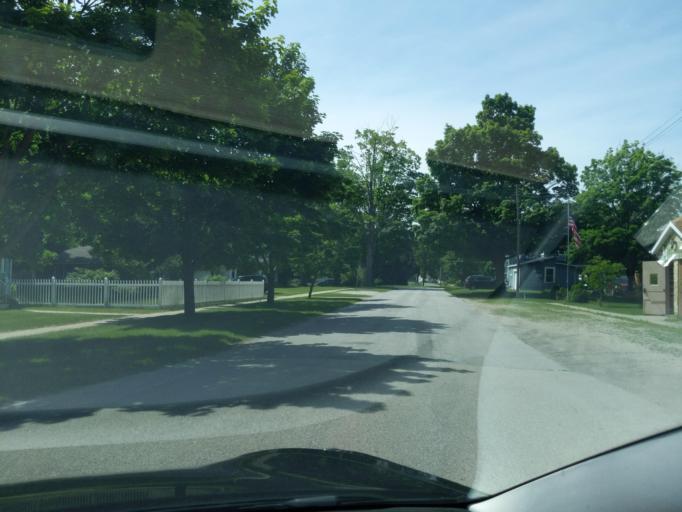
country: US
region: Michigan
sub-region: Muskegon County
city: Montague
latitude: 43.4169
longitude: -86.3584
